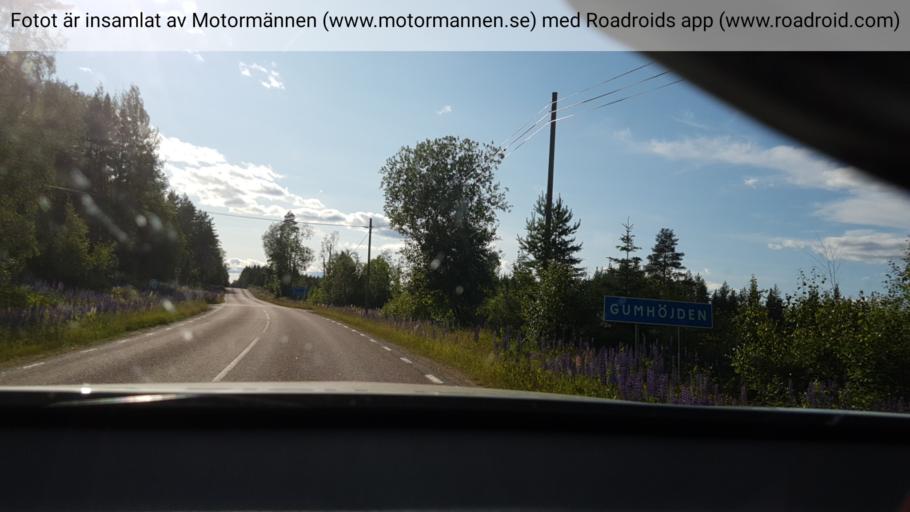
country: SE
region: Vaermland
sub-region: Hagfors Kommun
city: Hagfors
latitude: 60.0216
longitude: 13.9116
